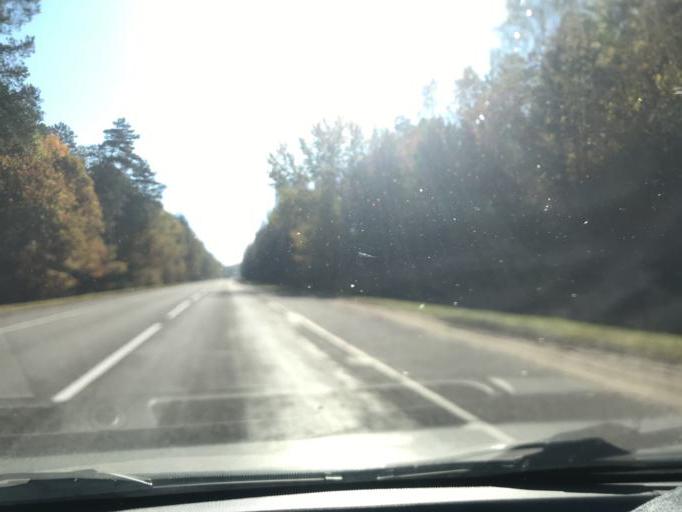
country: BY
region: Gomel
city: Kastsyukowka
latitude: 52.4308
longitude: 30.8273
